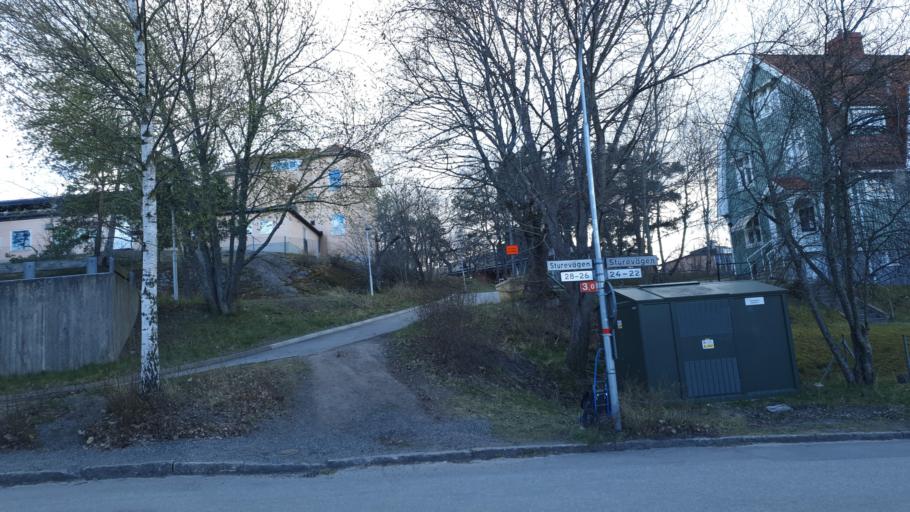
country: SE
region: Stockholm
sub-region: Lidingo
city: Lidingoe
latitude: 59.3668
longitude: 18.1283
